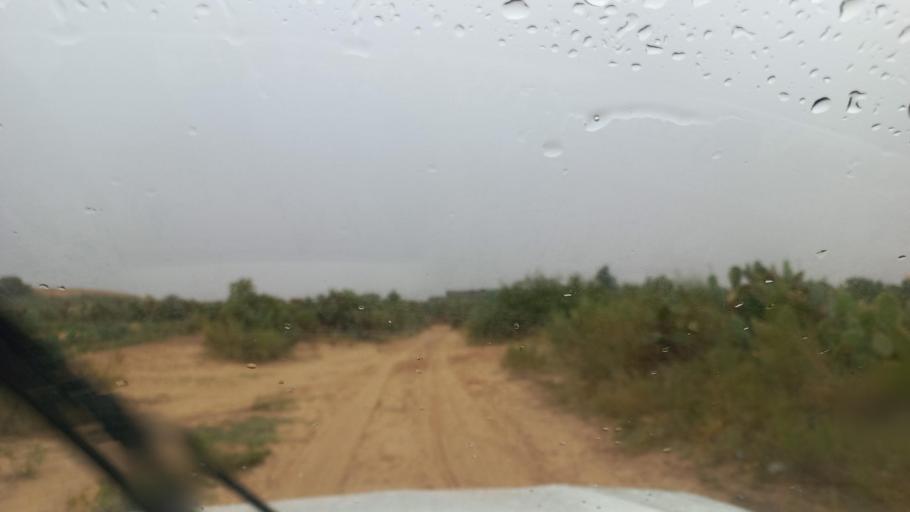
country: TN
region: Al Qasrayn
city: Kasserine
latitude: 35.2719
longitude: 8.9441
